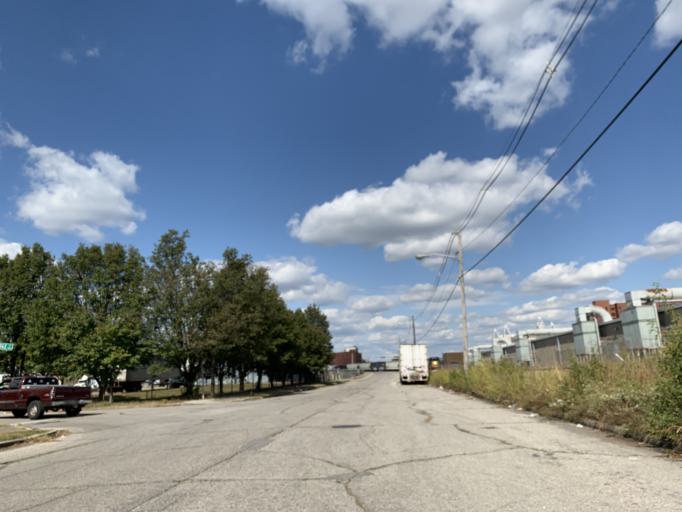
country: US
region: Kentucky
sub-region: Jefferson County
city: Louisville
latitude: 38.2431
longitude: -85.7705
